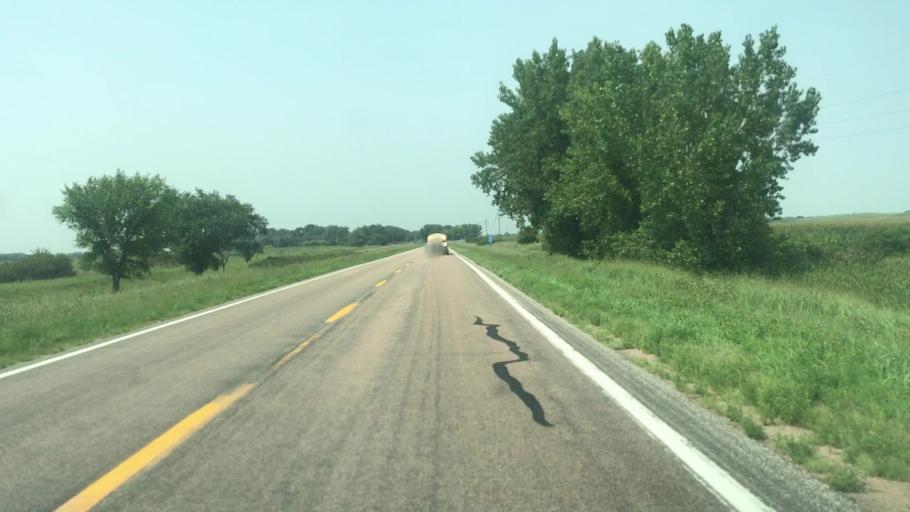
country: US
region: Nebraska
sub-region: Sherman County
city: Loup City
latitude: 41.2285
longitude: -98.9328
